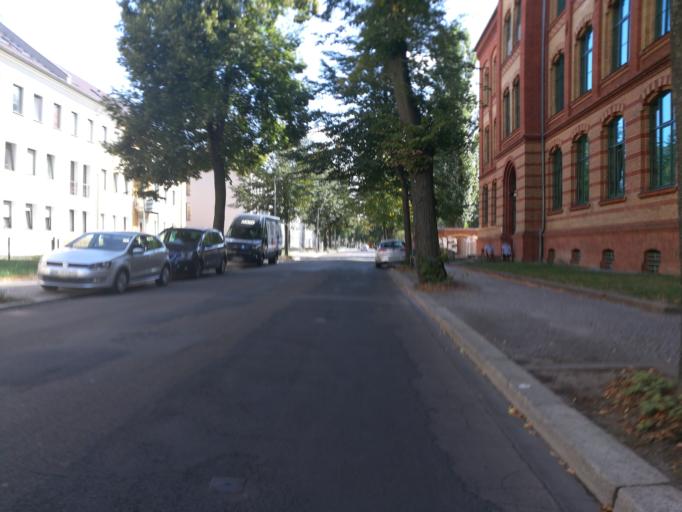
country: DE
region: Saxony-Anhalt
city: Magdeburg
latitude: 52.1315
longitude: 11.6086
